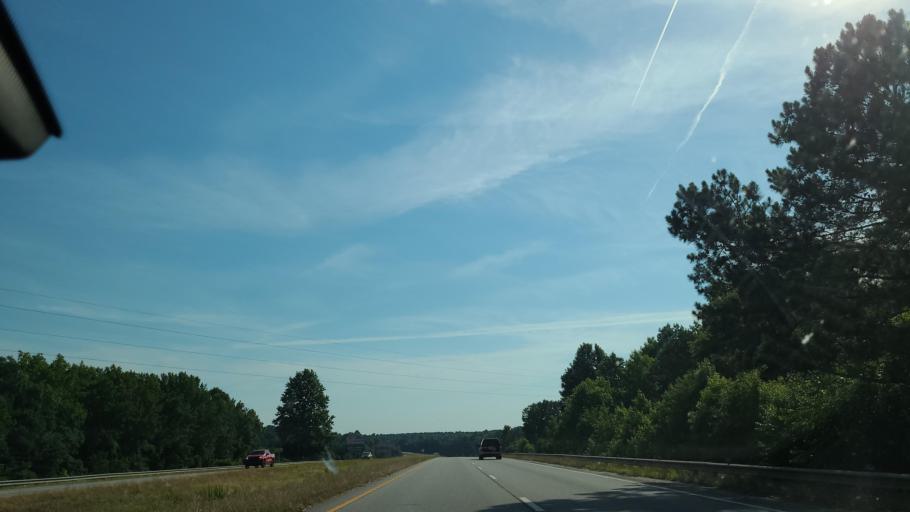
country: US
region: Georgia
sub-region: Jackson County
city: Commerce
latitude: 34.1837
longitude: -83.4394
